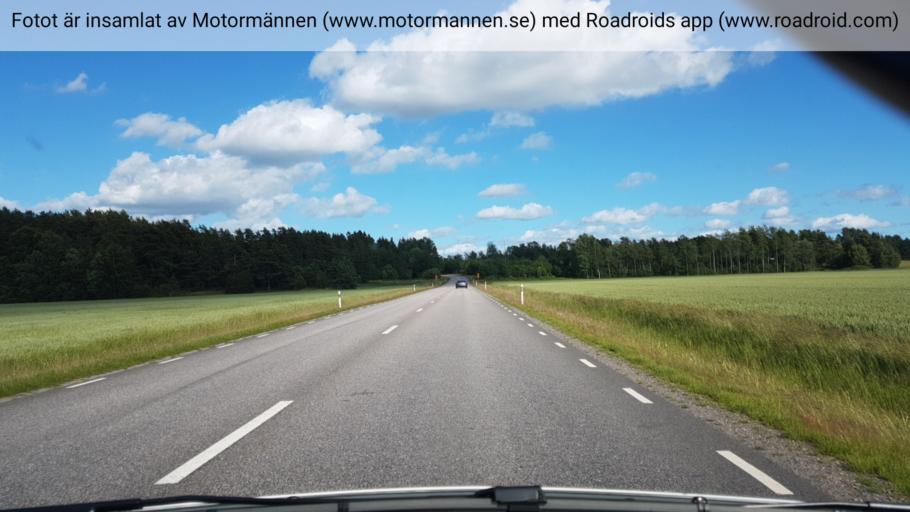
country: SE
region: Vaestra Goetaland
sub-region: Grastorps Kommun
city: Graestorp
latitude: 58.3243
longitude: 12.7413
